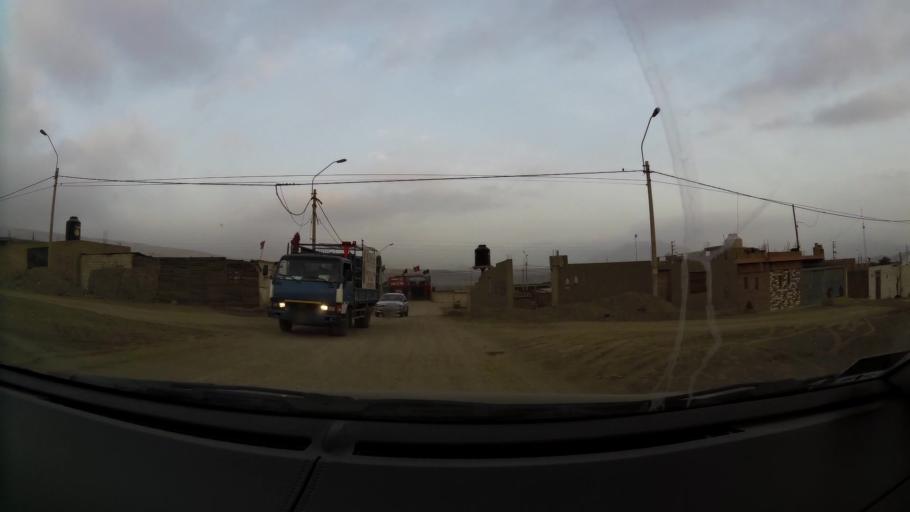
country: PE
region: Lima
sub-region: Lima
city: Santa Rosa
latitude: -11.7341
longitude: -77.1404
